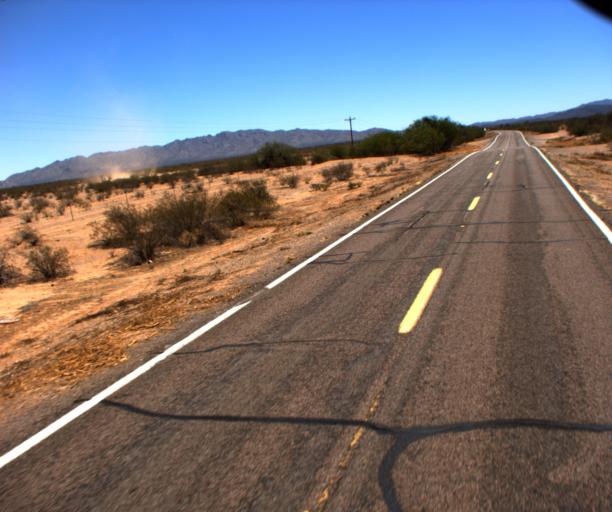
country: US
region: Arizona
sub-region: Pima County
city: Sells
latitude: 32.1829
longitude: -112.3505
